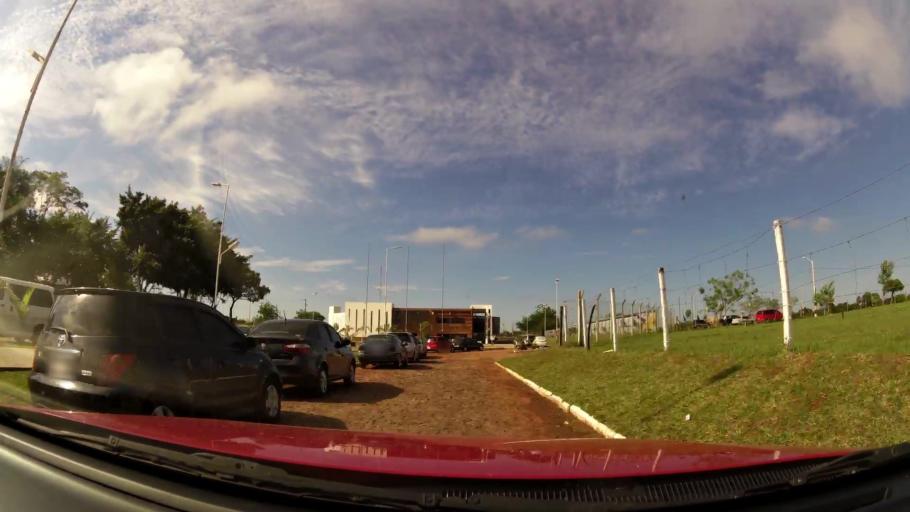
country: PY
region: Central
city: San Lorenzo
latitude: -25.2828
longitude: -57.4882
